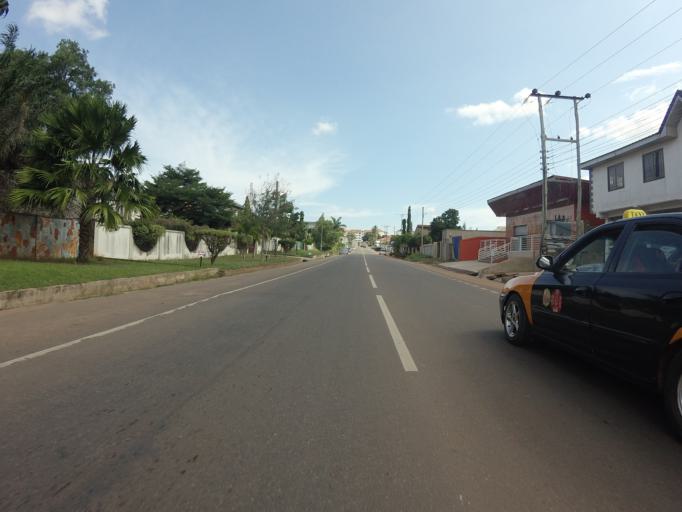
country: GH
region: Greater Accra
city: Medina Estates
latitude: 5.6712
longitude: -0.1820
